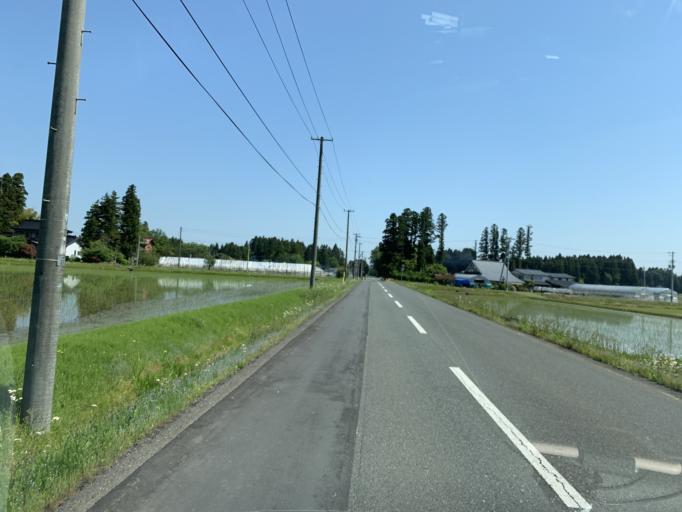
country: JP
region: Iwate
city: Mizusawa
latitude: 39.0837
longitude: 141.0671
